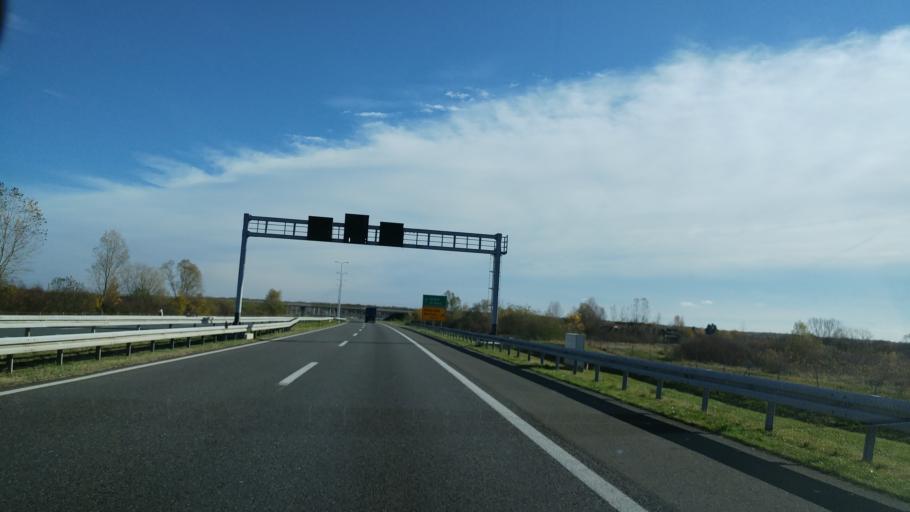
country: HR
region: Brodsko-Posavska
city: Okucani
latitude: 45.2323
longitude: 17.2032
